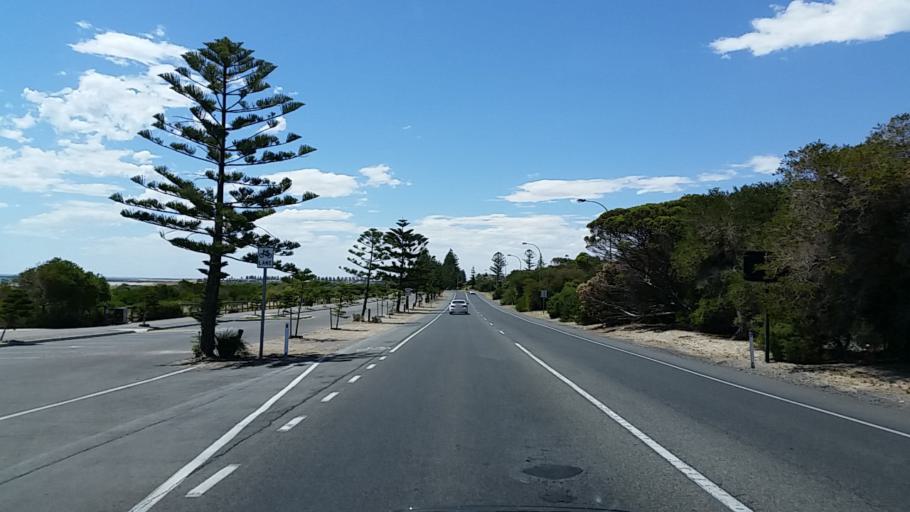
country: AU
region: South Australia
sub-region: Port Adelaide Enfield
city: Birkenhead
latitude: -34.8119
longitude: 138.4912
